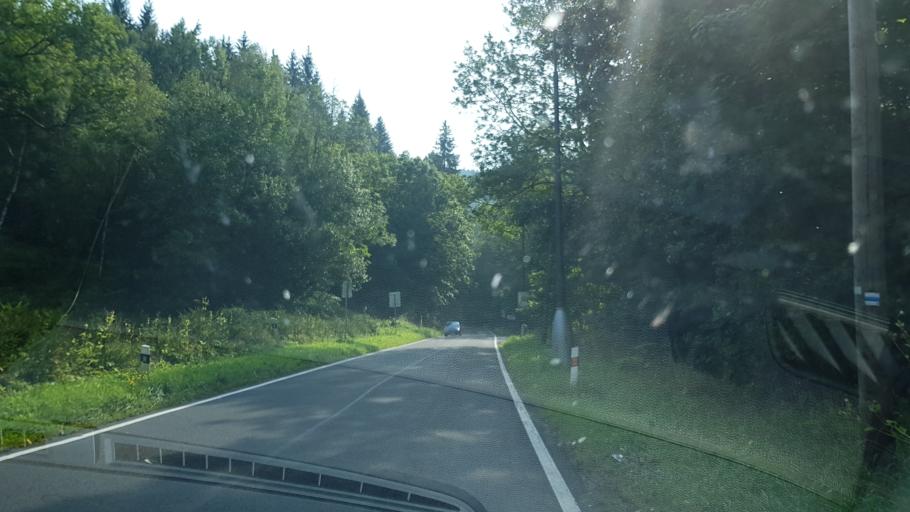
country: CZ
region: Olomoucky
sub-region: Okres Jesenik
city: Jesenik
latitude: 50.2059
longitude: 17.2352
